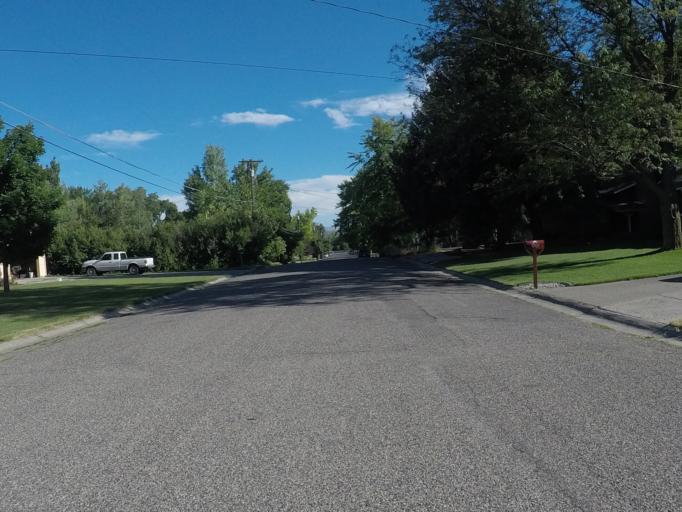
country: US
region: Montana
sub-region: Yellowstone County
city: Billings
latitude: 45.7946
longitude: -108.5846
